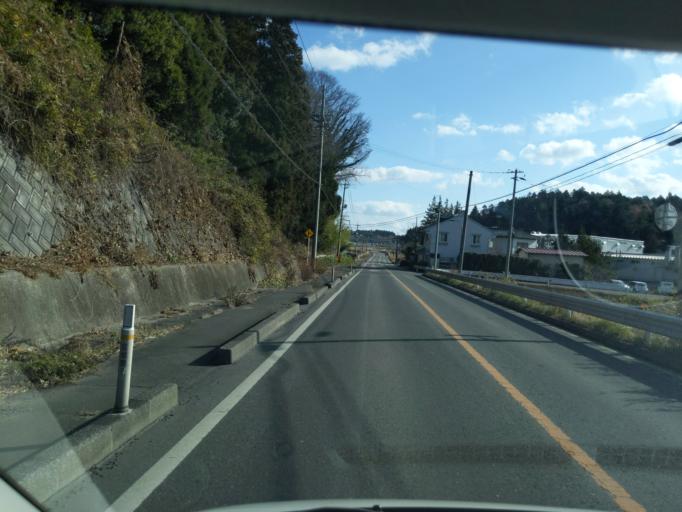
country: JP
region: Miyagi
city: Kogota
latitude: 38.7326
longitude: 141.0466
